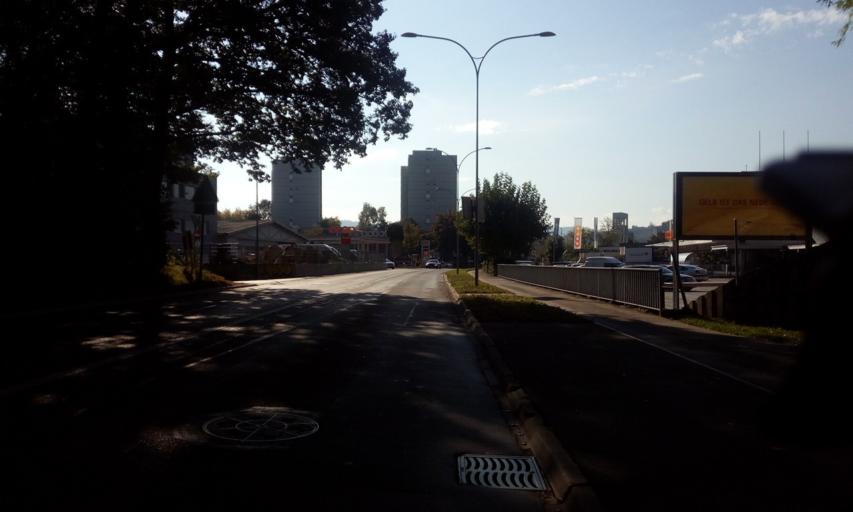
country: CH
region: Bern
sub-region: Bern-Mittelland District
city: Koniz
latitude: 46.9518
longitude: 7.3921
